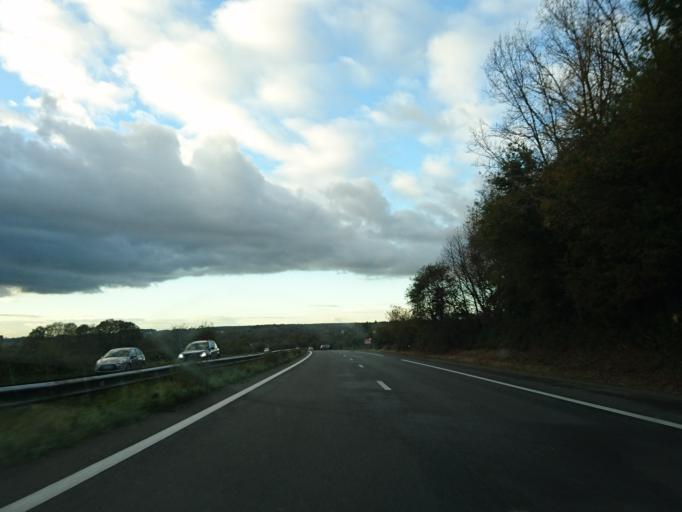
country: FR
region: Brittany
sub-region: Departement d'Ille-et-Vilaine
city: Montauban-de-Bretagne
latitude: 48.2050
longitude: -2.0359
